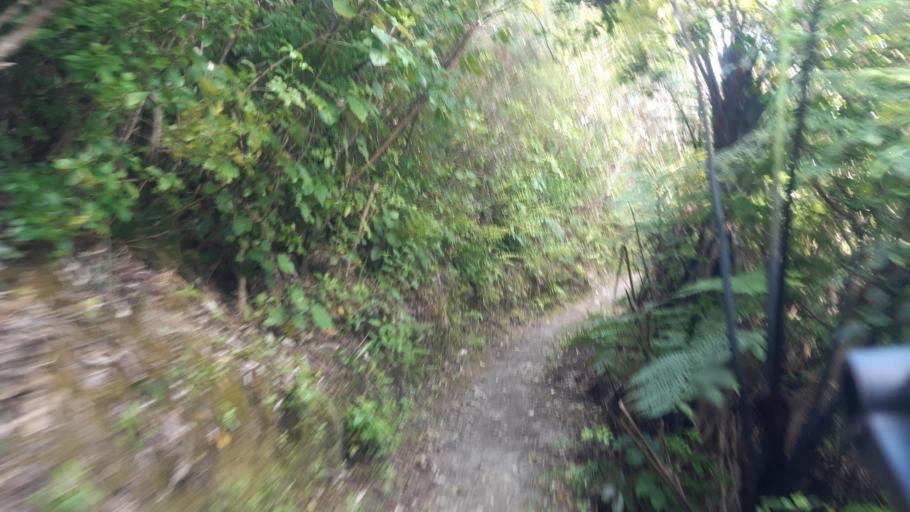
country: NZ
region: Marlborough
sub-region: Marlborough District
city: Picton
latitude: -41.2780
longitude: 174.0175
